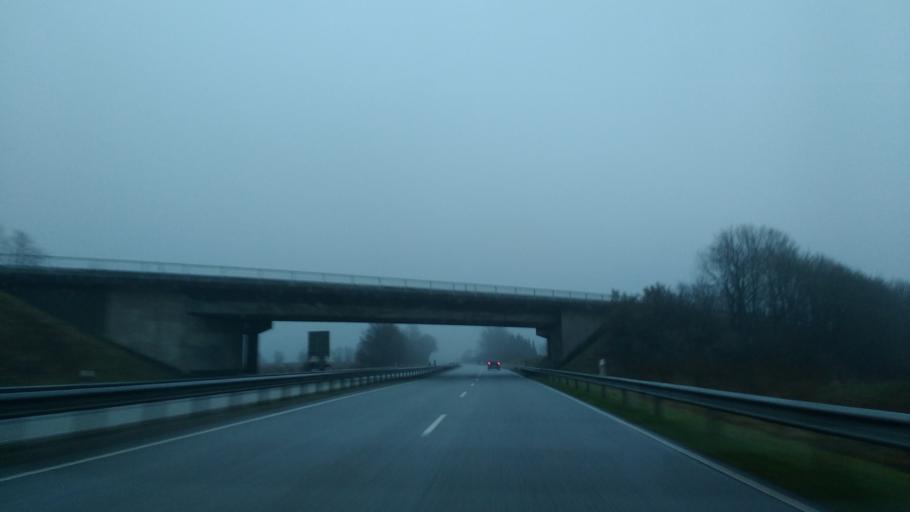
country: DE
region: Schleswig-Holstein
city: Jevenstedt
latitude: 54.2529
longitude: 9.6669
